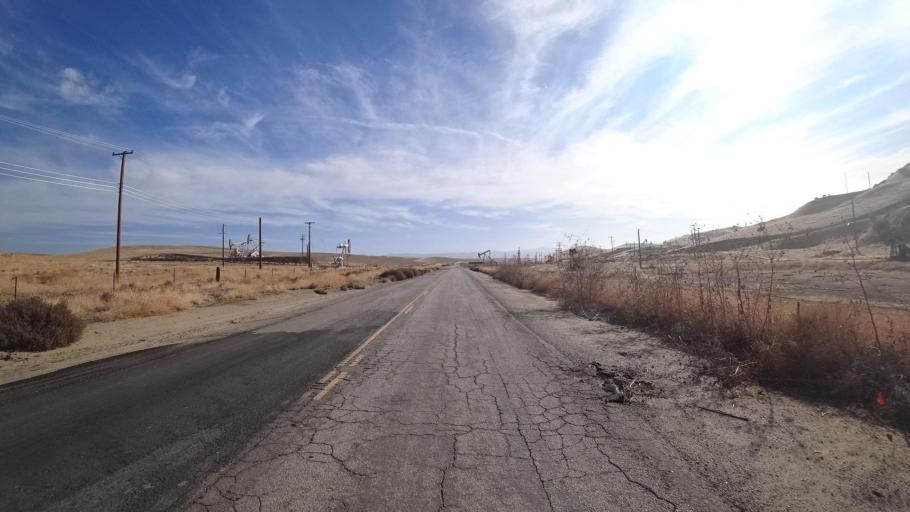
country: US
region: California
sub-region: Kern County
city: Oildale
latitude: 35.6119
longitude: -118.9735
